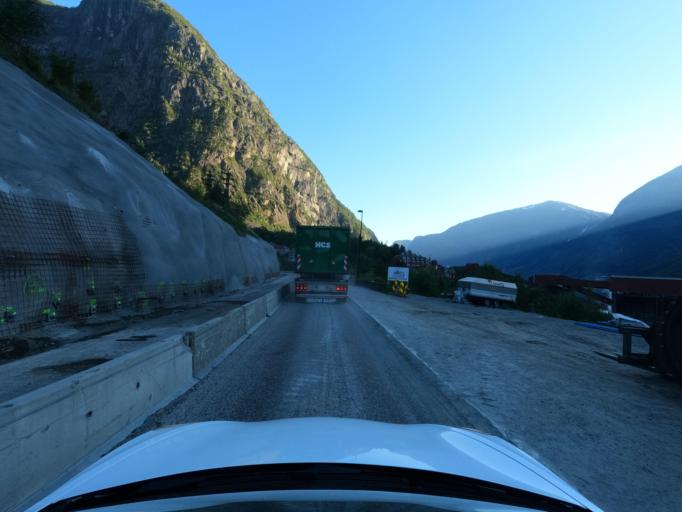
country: NO
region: Hordaland
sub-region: Odda
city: Odda
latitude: 60.1188
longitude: 6.5579
